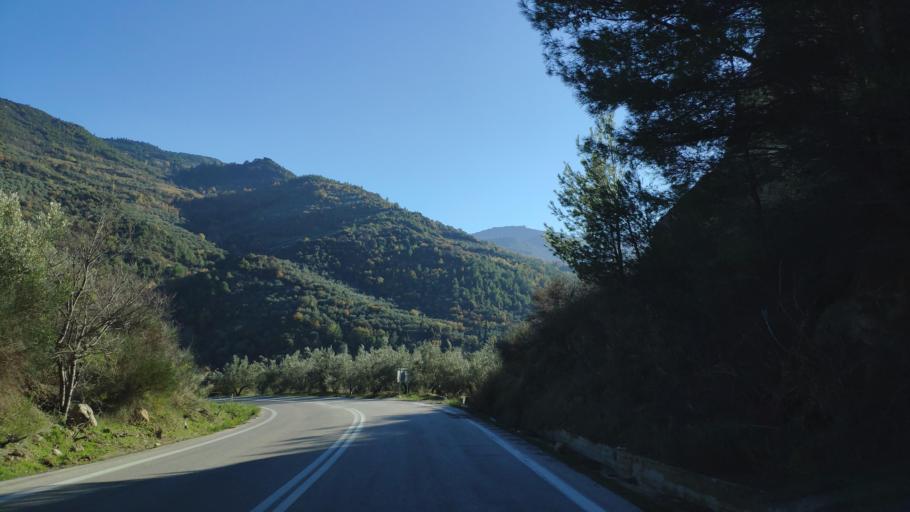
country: GR
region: Peloponnese
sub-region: Nomos Korinthias
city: Xylokastro
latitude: 38.0017
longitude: 22.5039
